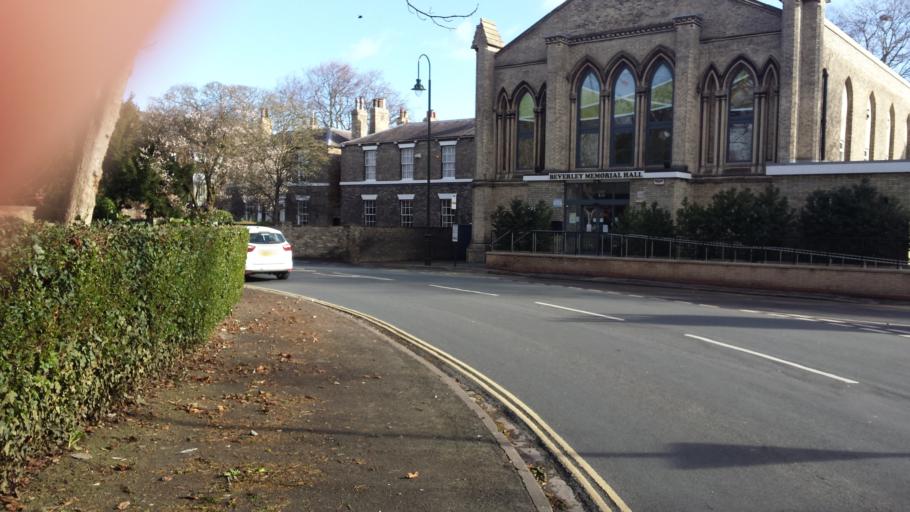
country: GB
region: England
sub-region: East Riding of Yorkshire
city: Beverley
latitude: 53.8395
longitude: -0.4311
